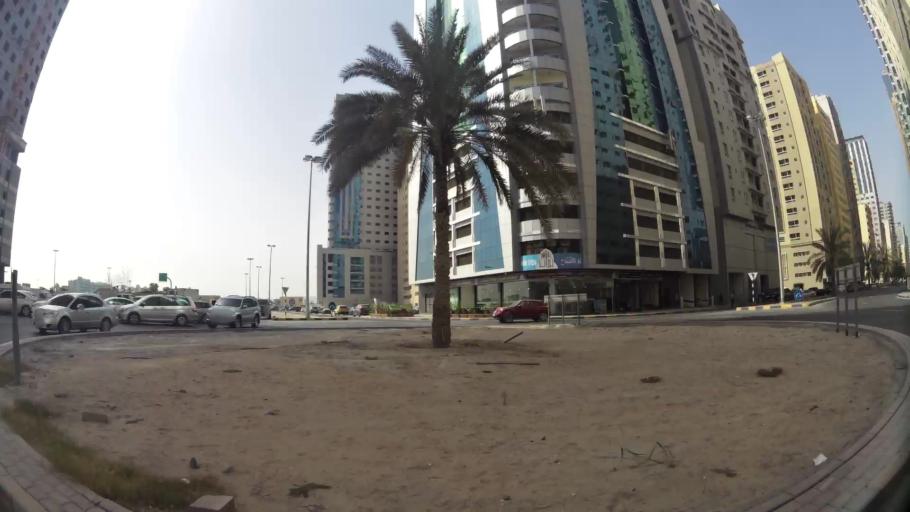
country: AE
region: Ash Shariqah
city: Sharjah
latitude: 25.3152
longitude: 55.3786
